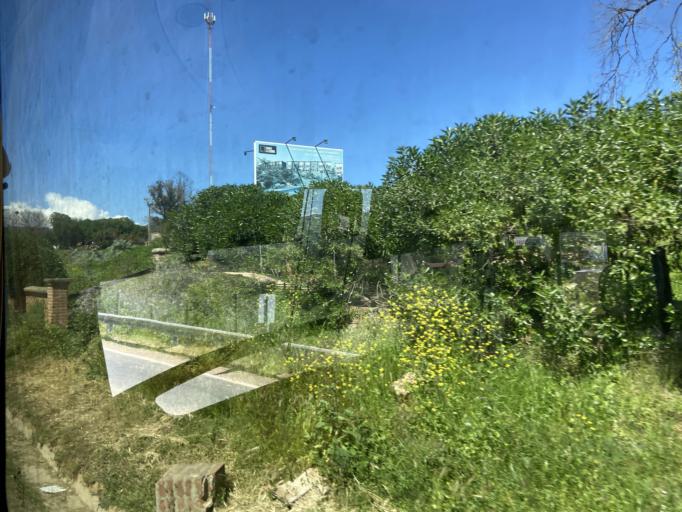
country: CL
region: Valparaiso
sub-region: Provincia de Marga Marga
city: Villa Alemana
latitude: -33.1536
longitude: -71.3329
